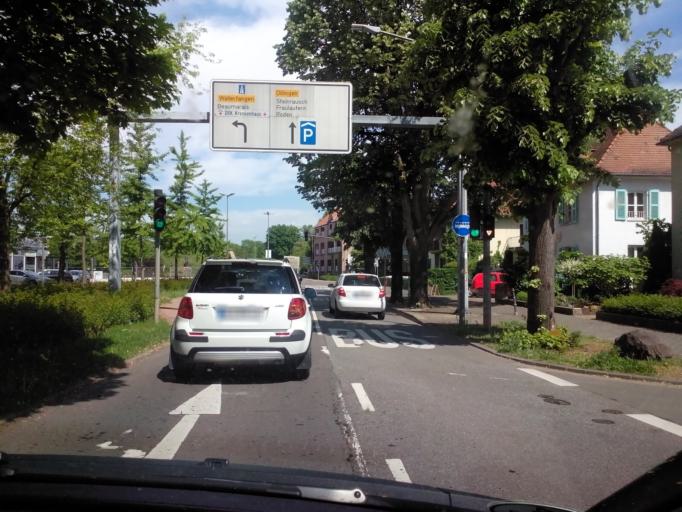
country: DE
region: Saarland
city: Saarlouis
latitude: 49.3139
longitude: 6.7471
